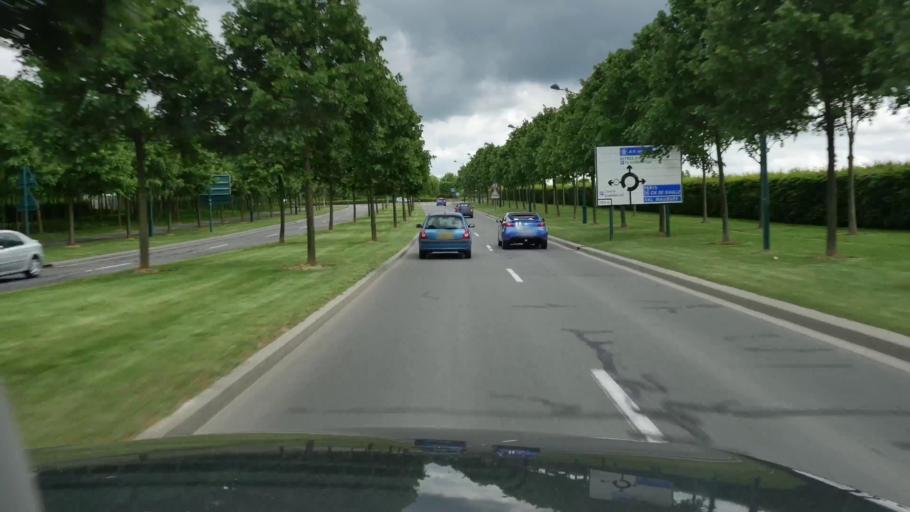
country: FR
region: Ile-de-France
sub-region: Departement de Seine-et-Marne
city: Serris
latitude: 48.8528
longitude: 2.7759
